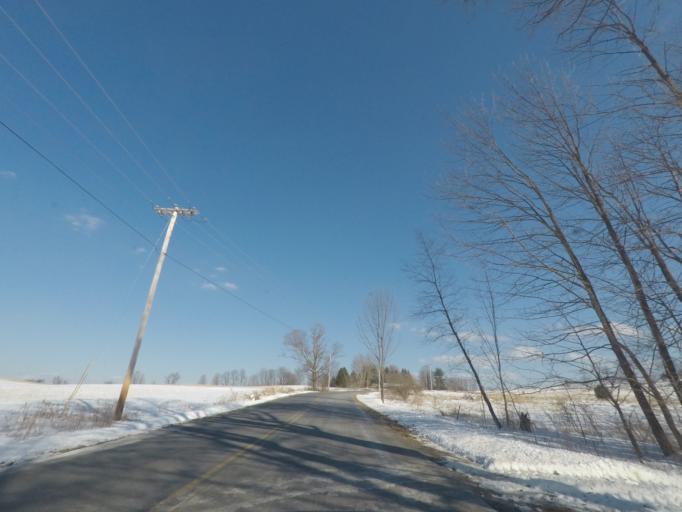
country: US
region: New York
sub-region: Rensselaer County
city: Hoosick Falls
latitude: 42.8711
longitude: -73.4960
